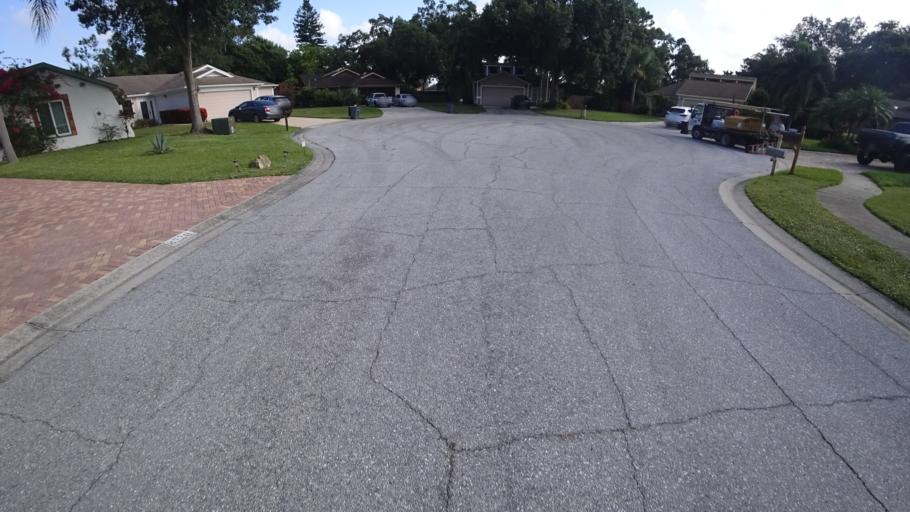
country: US
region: Florida
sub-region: Sarasota County
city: North Sarasota
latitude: 27.3935
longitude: -82.5031
